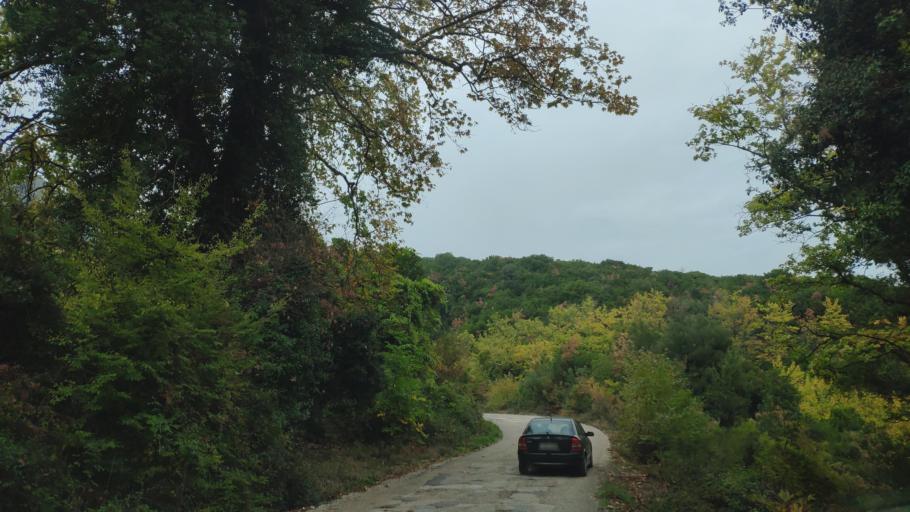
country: GR
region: Epirus
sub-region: Nomos Thesprotias
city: Paramythia
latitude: 39.4675
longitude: 20.6716
